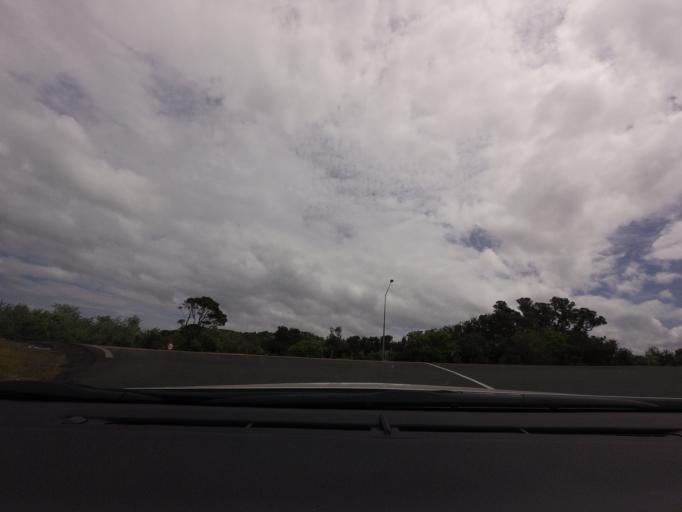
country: NZ
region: Auckland
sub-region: Auckland
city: Warkworth
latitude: -36.5375
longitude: 174.7039
